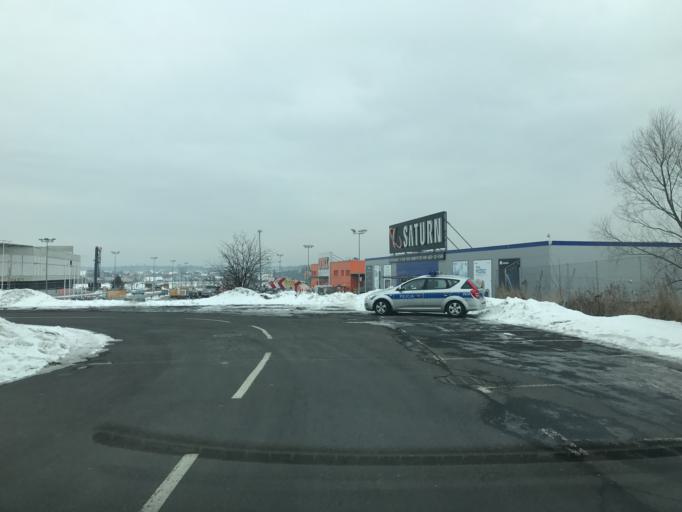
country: PL
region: Silesian Voivodeship
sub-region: Tychy
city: Cielmice
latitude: 50.0979
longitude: 19.0071
